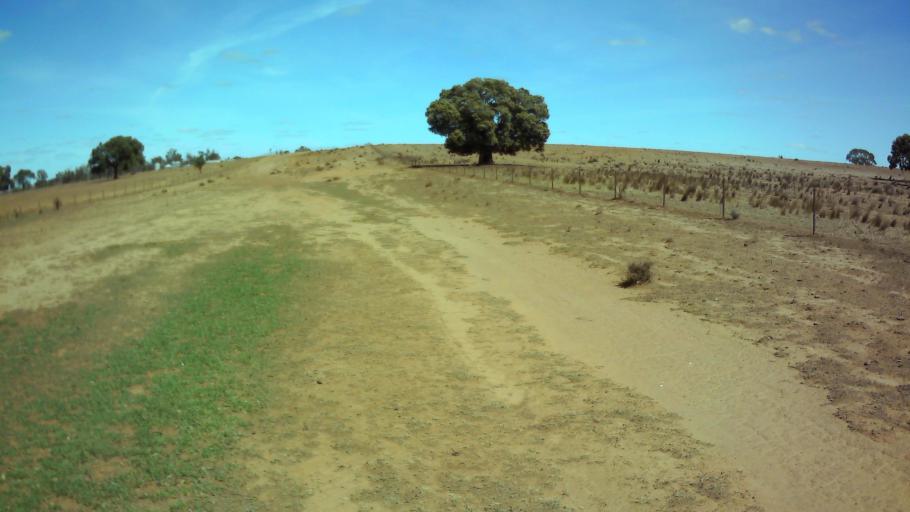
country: AU
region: New South Wales
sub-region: Forbes
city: Forbes
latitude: -33.7175
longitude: 147.8166
